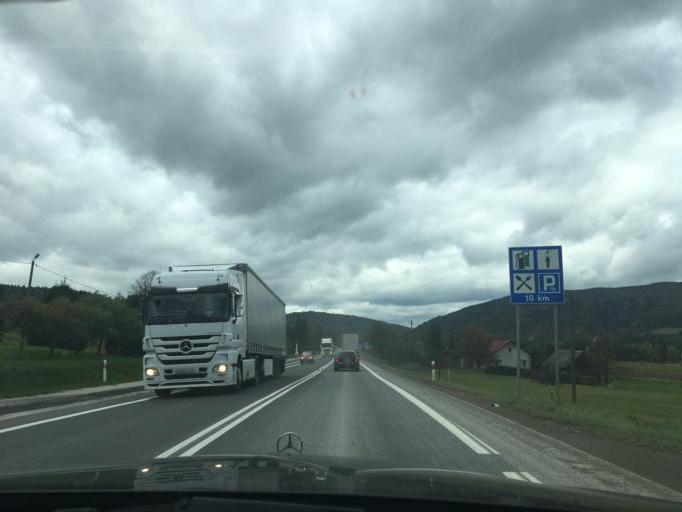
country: PL
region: Subcarpathian Voivodeship
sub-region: Powiat krosnienski
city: Dukla
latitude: 49.4982
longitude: 21.7007
